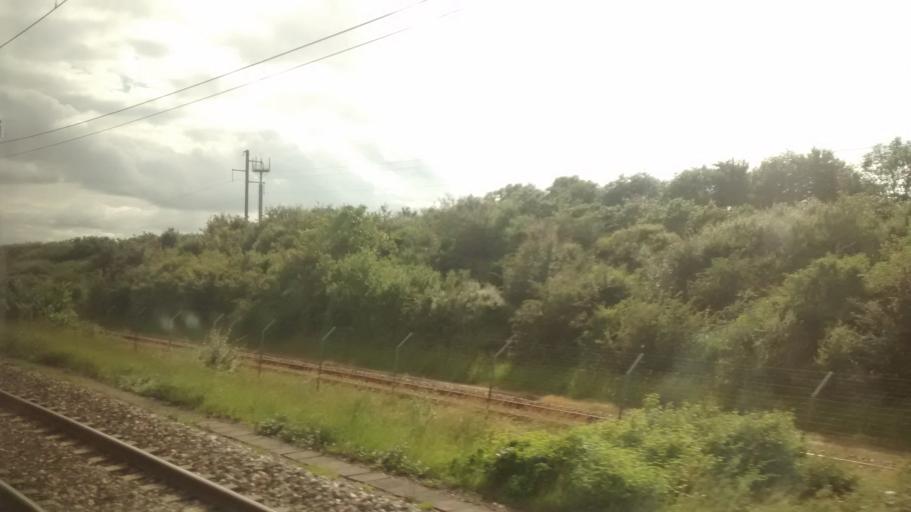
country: FR
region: Centre
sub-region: Departement d'Eure-et-Loir
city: Auneau
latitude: 48.4212
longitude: 1.7584
